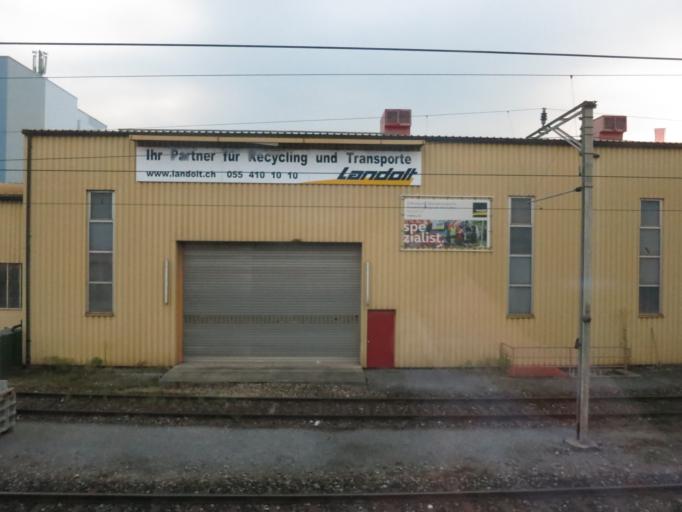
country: CH
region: Schwyz
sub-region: Bezirk Hoefe
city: Freienbach
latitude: 47.2023
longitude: 8.7933
